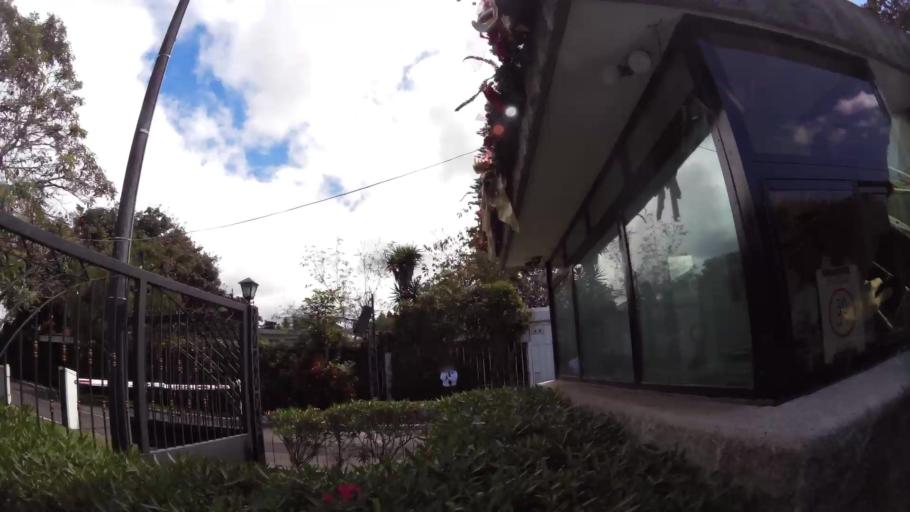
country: GT
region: Guatemala
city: Santa Catarina Pinula
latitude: 14.5781
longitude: -90.5171
